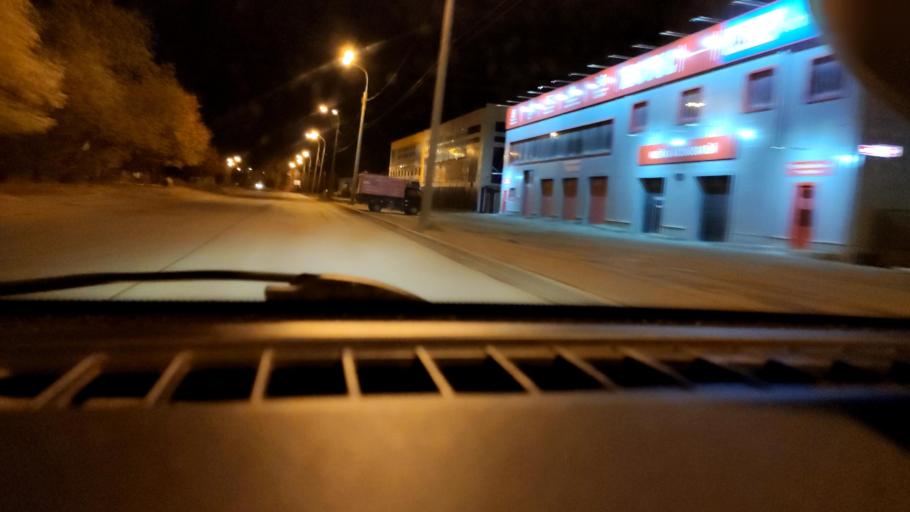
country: RU
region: Samara
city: Samara
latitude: 53.1344
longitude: 50.1167
